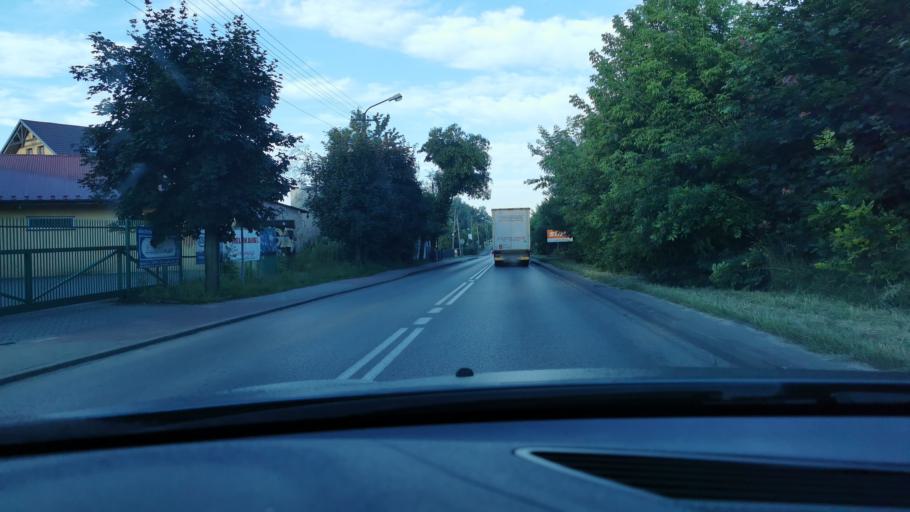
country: PL
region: Lesser Poland Voivodeship
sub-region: Powiat chrzanowski
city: Chrzanow
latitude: 50.1381
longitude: 19.4062
